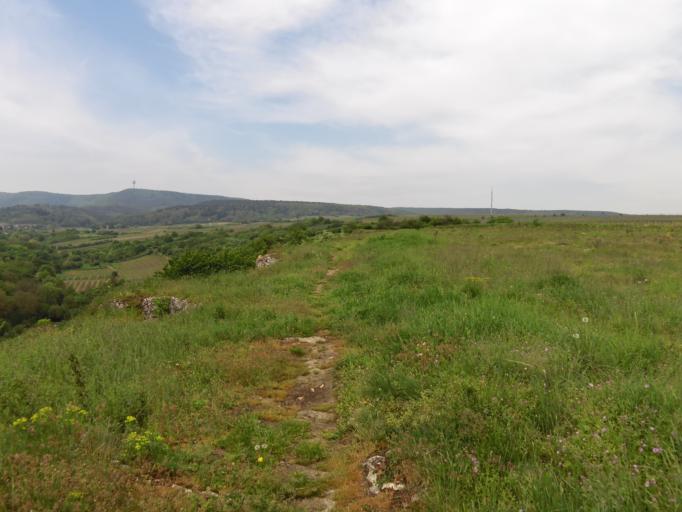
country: DE
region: Rheinland-Pfalz
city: Herxheim am Berg
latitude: 49.5026
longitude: 8.1699
